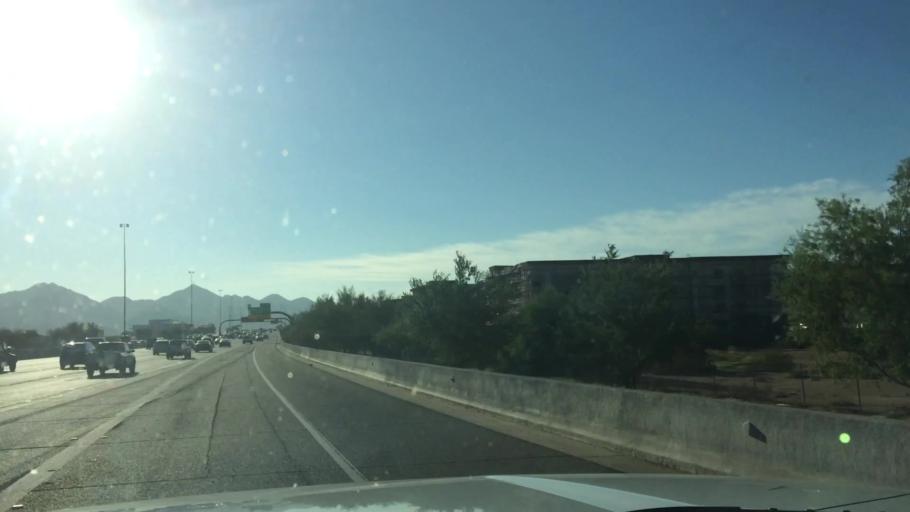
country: US
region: Arizona
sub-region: Maricopa County
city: Paradise Valley
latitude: 33.6628
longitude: -111.9362
